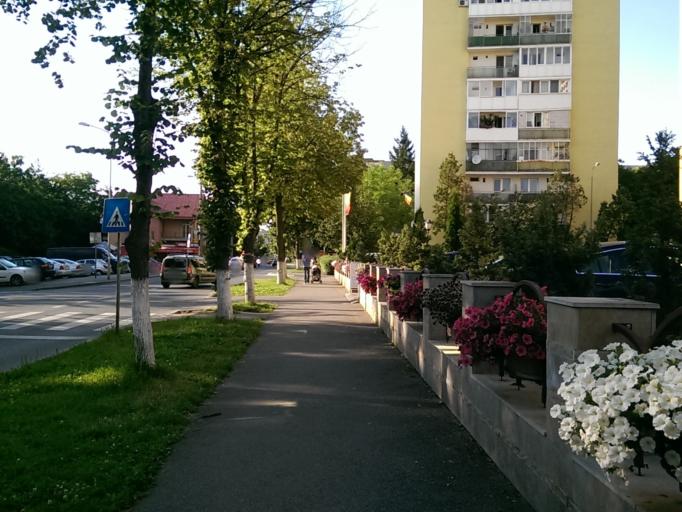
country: RO
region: Cluj
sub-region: Municipiul Cluj-Napoca
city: Cluj-Napoca
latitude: 46.7639
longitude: 23.6208
